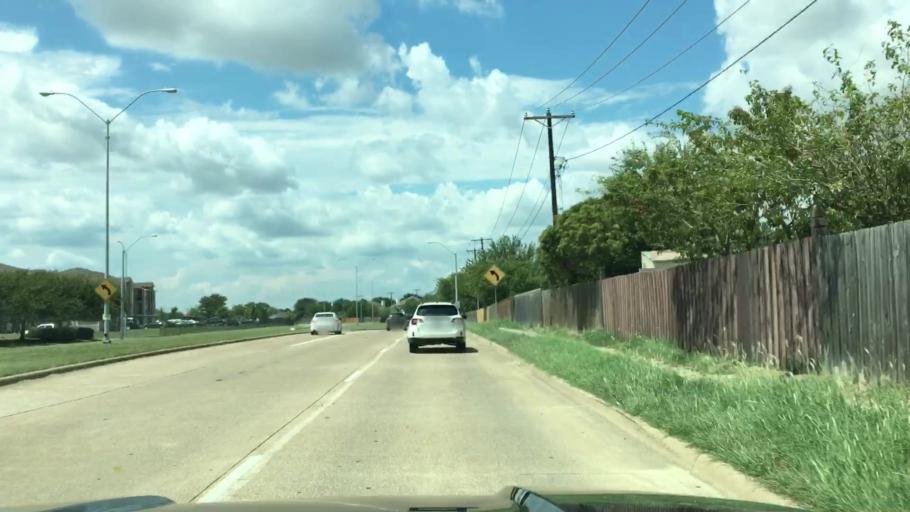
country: US
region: Texas
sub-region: Tarrant County
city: Blue Mound
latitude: 32.8622
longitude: -97.3355
